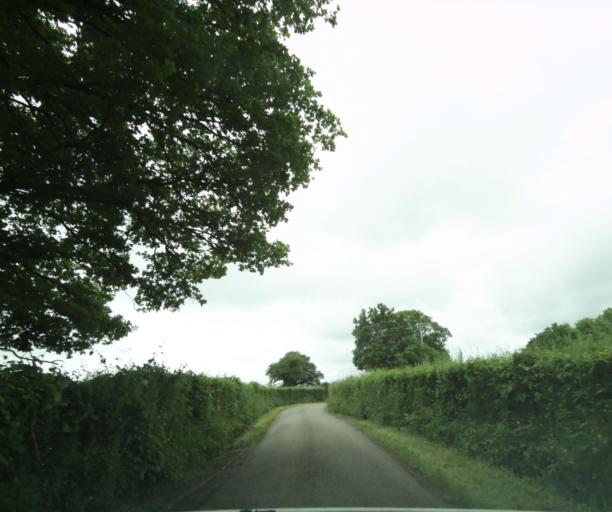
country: FR
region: Bourgogne
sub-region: Departement de Saone-et-Loire
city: Charolles
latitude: 46.4465
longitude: 4.2801
